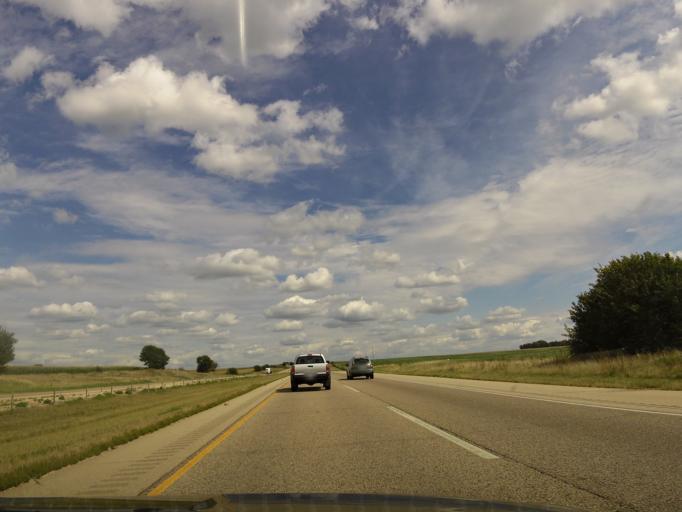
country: US
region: Illinois
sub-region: Ogle County
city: Rochelle
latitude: 41.9053
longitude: -88.9907
